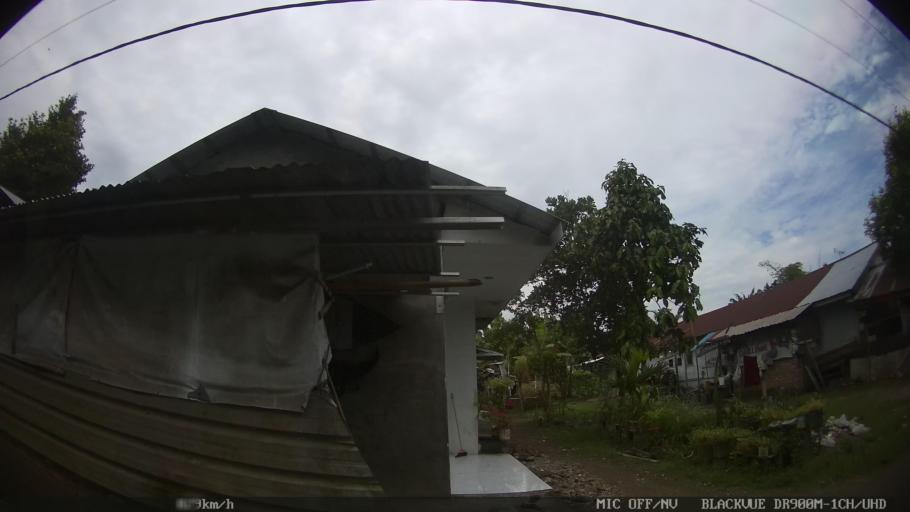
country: ID
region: North Sumatra
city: Sunggal
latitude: 3.6497
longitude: 98.5922
